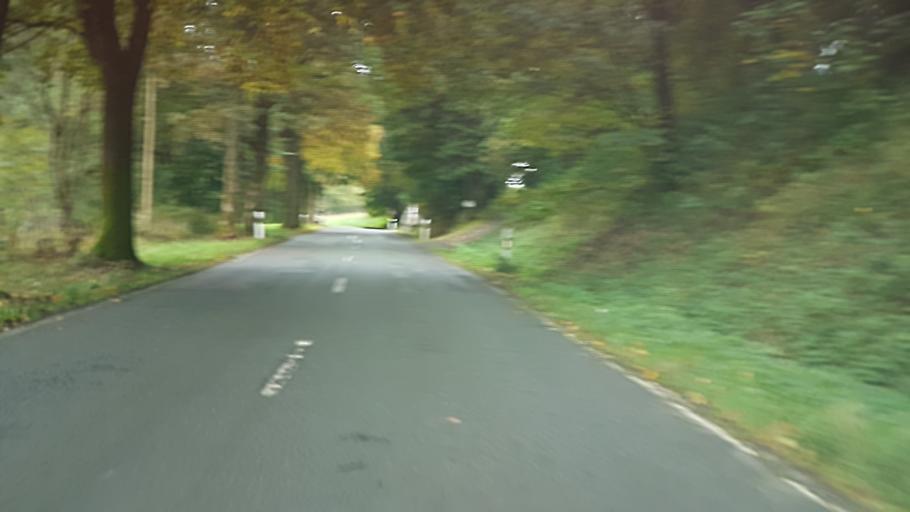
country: DE
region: North Rhine-Westphalia
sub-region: Regierungsbezirk Arnsberg
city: Herscheid
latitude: 51.1542
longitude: 7.7006
